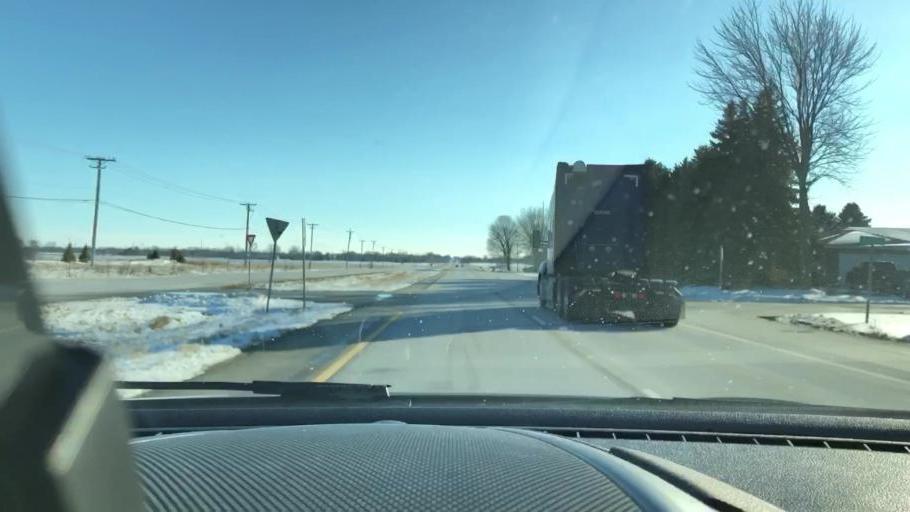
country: US
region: Illinois
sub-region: Will County
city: Preston Heights
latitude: 41.4495
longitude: -88.0792
